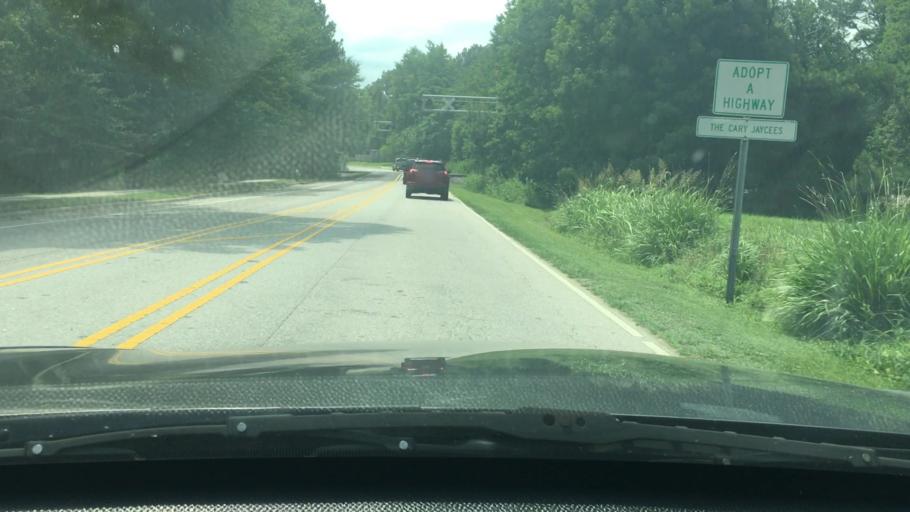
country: US
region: North Carolina
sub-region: Wake County
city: Cary
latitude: 35.7863
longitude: -78.7942
